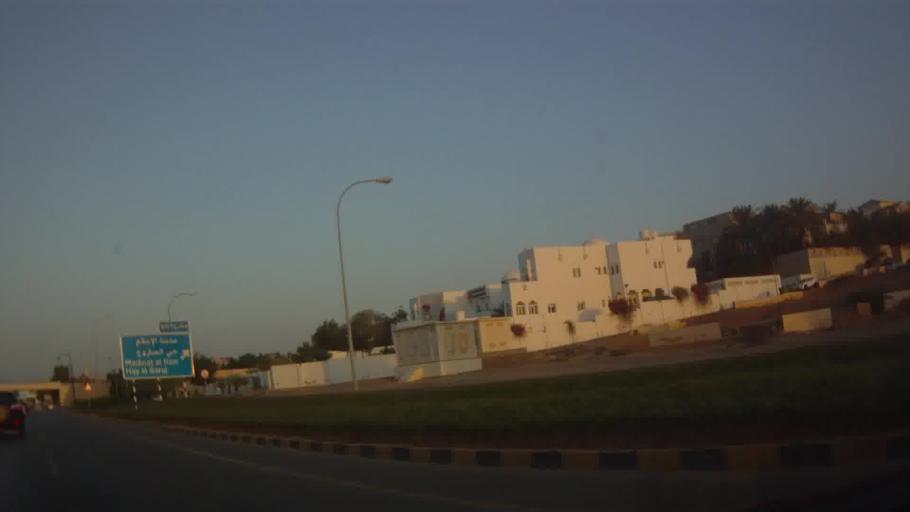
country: OM
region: Muhafazat Masqat
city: Bawshar
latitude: 23.6128
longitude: 58.4705
